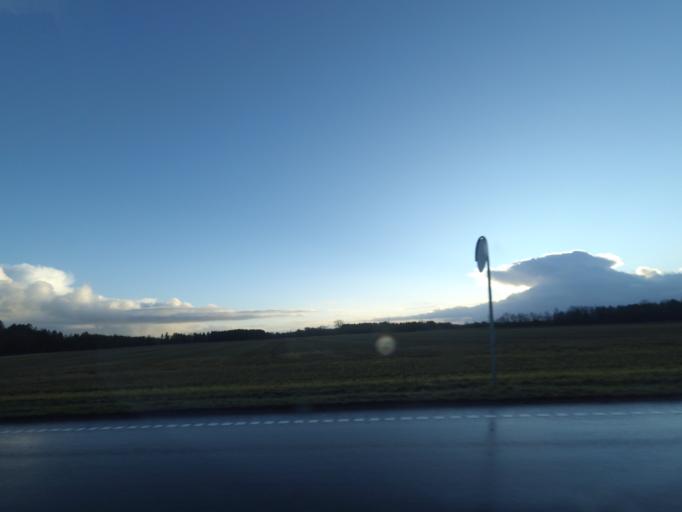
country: DK
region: Central Jutland
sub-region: Ikast-Brande Kommune
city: Brande
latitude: 56.0061
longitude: 9.1294
